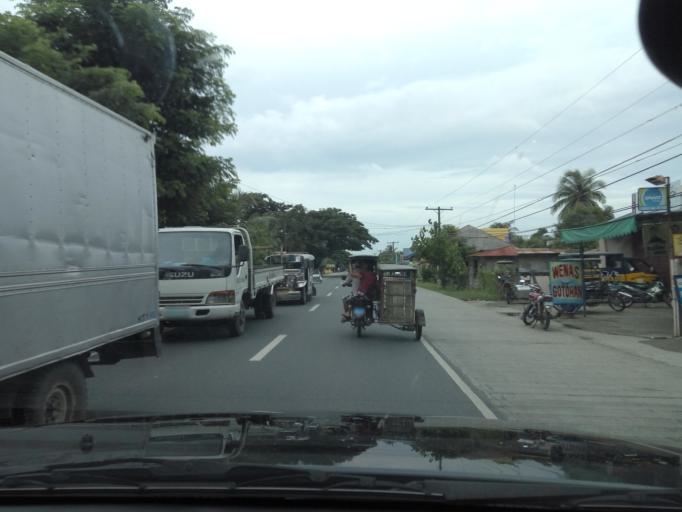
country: PH
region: Central Luzon
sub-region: Province of Nueva Ecija
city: Concepcion
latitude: 15.4480
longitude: 120.8095
